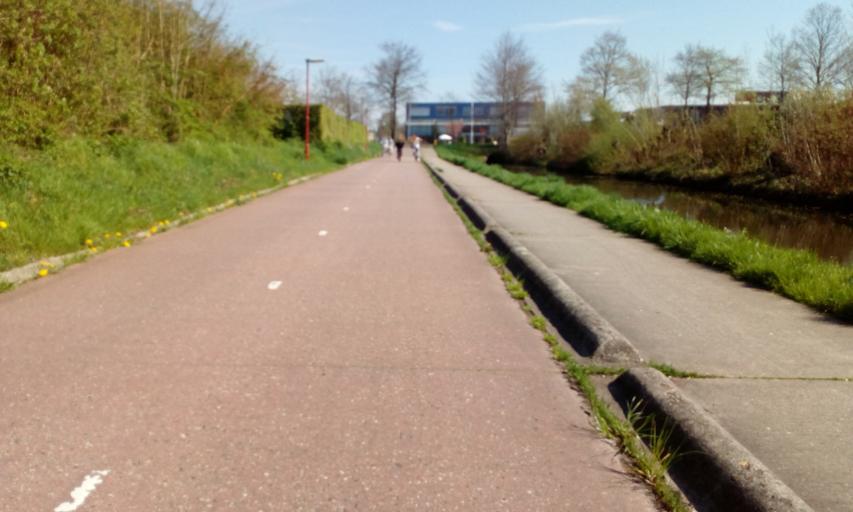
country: NL
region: South Holland
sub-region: Gemeente Rijnwoude
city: Benthuizen
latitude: 52.0701
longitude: 4.5188
